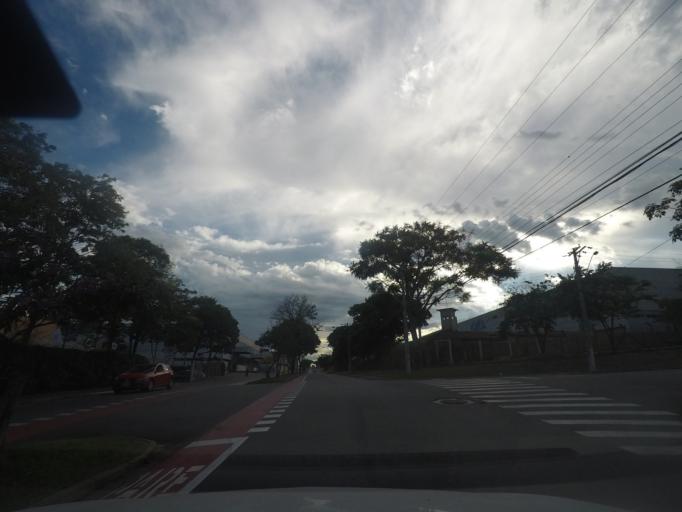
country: BR
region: Sao Paulo
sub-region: Taubate
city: Taubate
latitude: -23.0456
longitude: -45.5953
